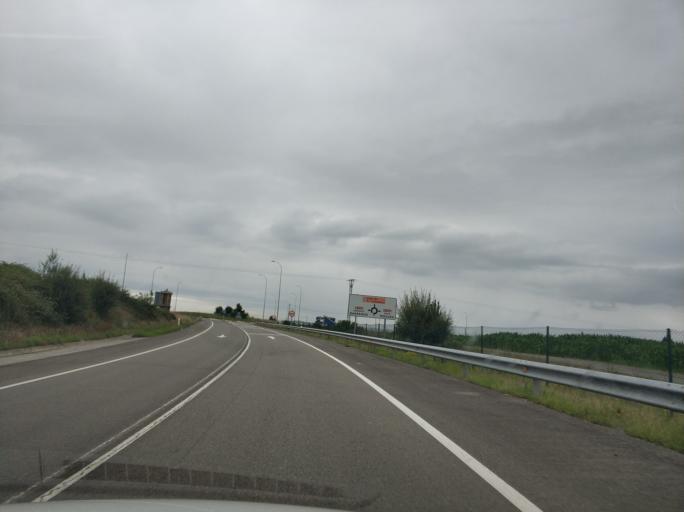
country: ES
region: Galicia
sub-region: Provincia de Lugo
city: Barreiros
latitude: 43.5457
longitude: -7.1513
